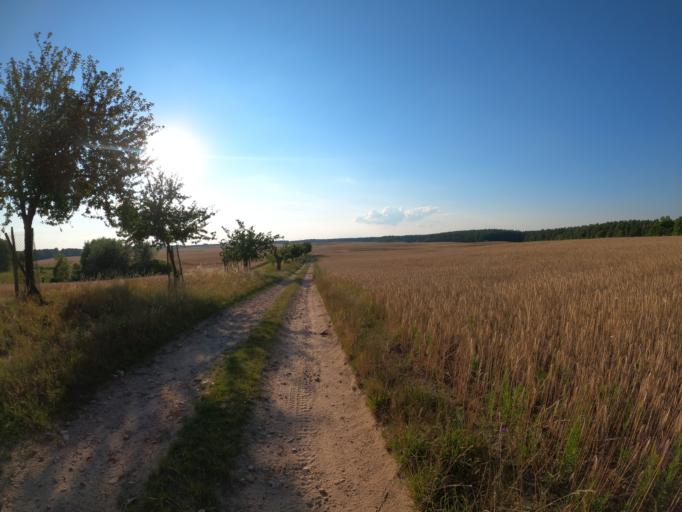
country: DE
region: Brandenburg
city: Althuttendorf
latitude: 53.0273
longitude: 13.8885
